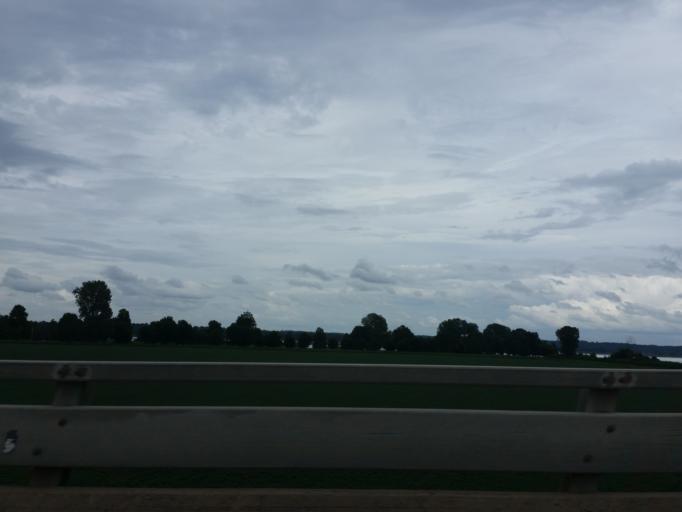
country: US
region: Illinois
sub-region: Alexander County
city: Cairo
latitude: 36.9835
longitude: -89.1493
